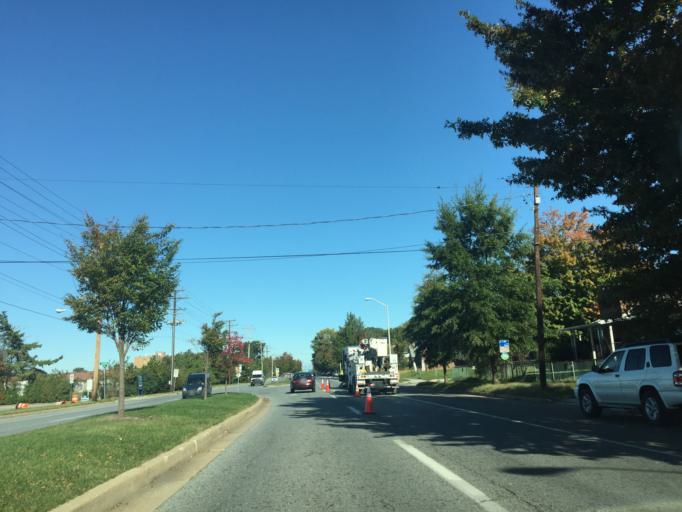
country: US
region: Maryland
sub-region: Baltimore County
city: Dundalk
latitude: 39.2521
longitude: -76.5212
